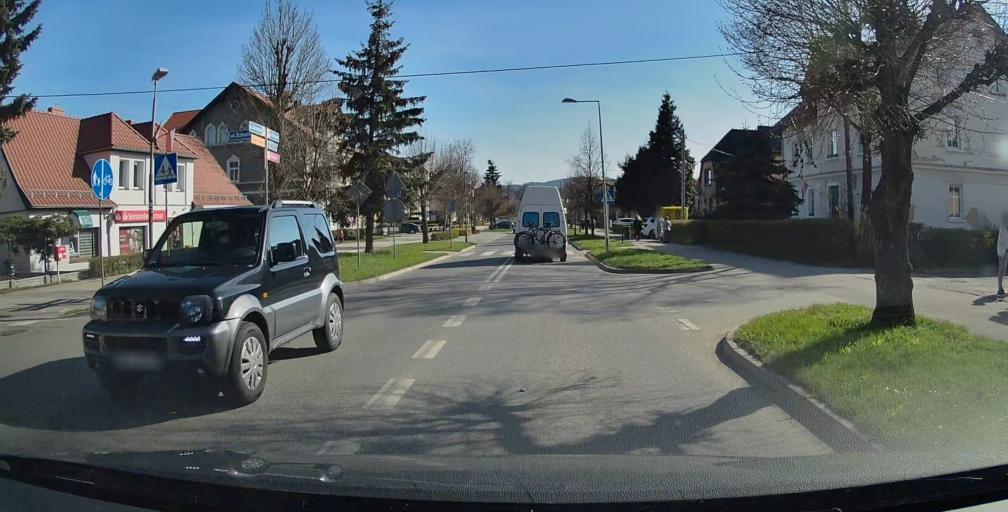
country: PL
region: Lower Silesian Voivodeship
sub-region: Powiat klodzki
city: Kudowa-Zdroj
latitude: 50.4387
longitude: 16.2398
